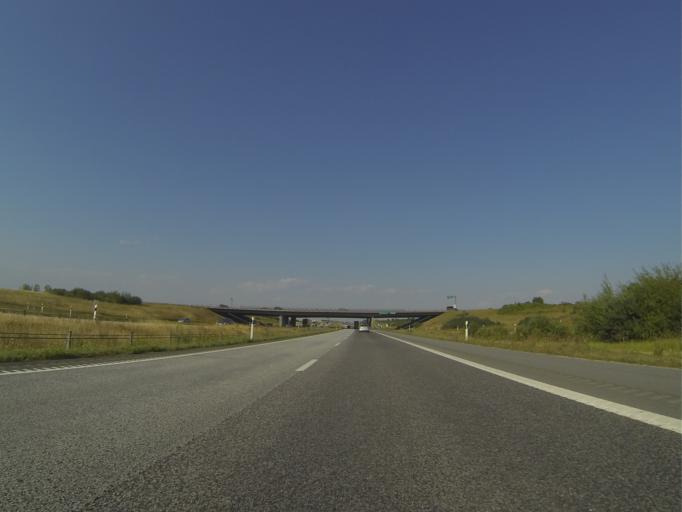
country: SE
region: Skane
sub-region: Malmo
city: Oxie
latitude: 55.5586
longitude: 13.0765
